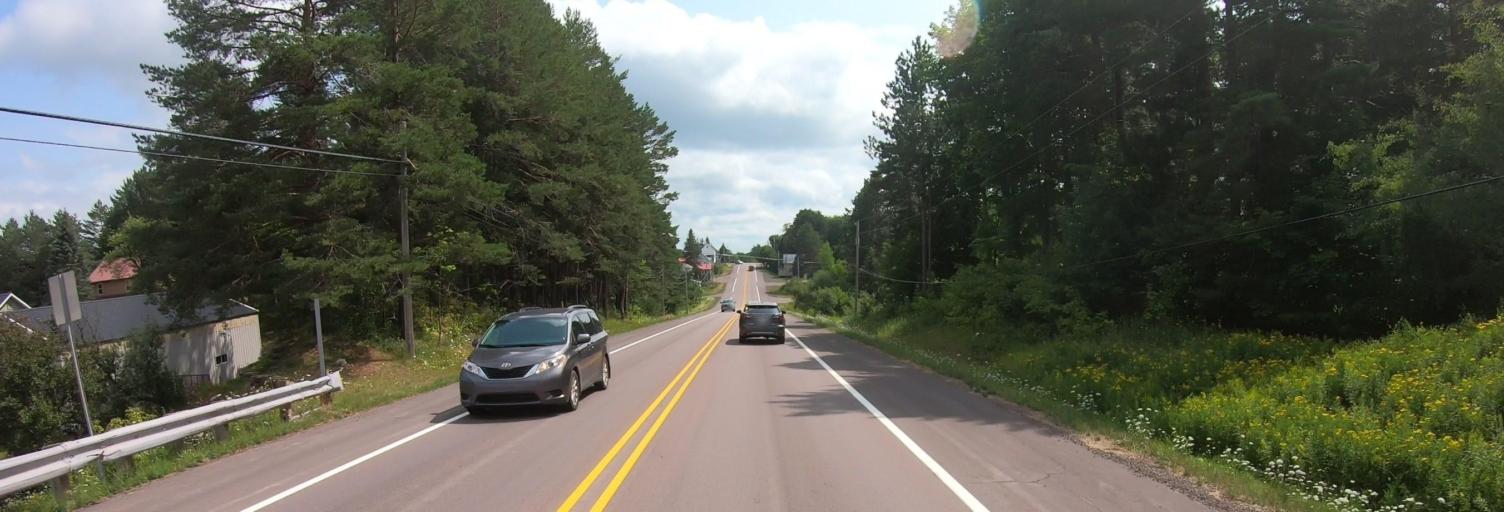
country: US
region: Michigan
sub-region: Houghton County
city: Hancock
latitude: 47.0450
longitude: -88.6726
